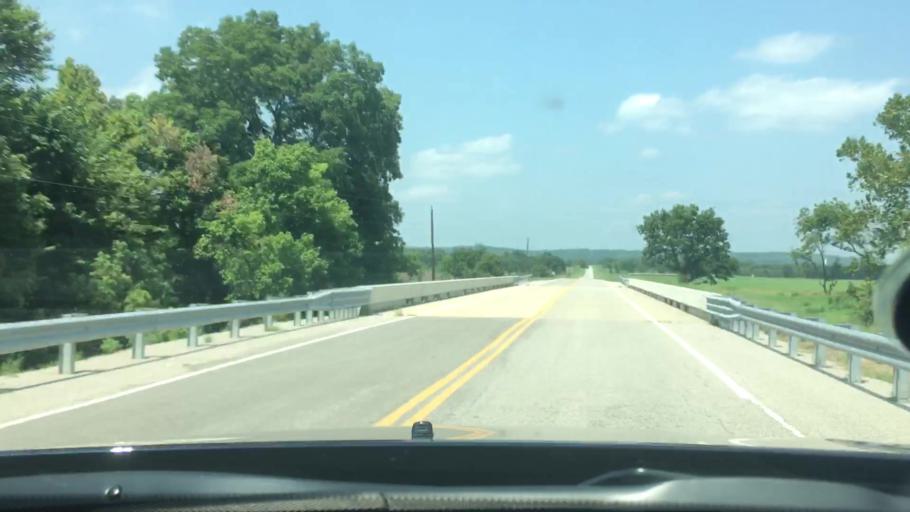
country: US
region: Oklahoma
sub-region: Johnston County
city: Tishomingo
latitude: 34.3891
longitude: -96.4962
